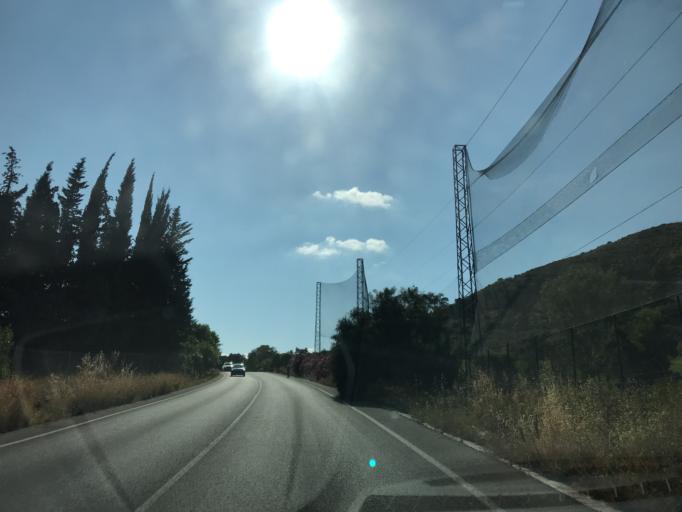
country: ES
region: Andalusia
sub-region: Provincia de Malaga
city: Benahavis
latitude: 36.5077
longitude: -5.0168
